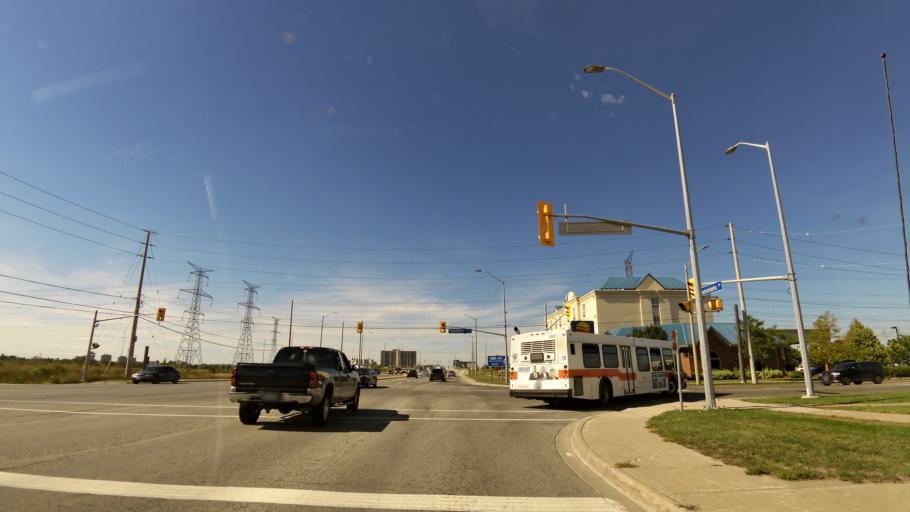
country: CA
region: Ontario
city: Brampton
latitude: 43.6500
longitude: -79.7114
